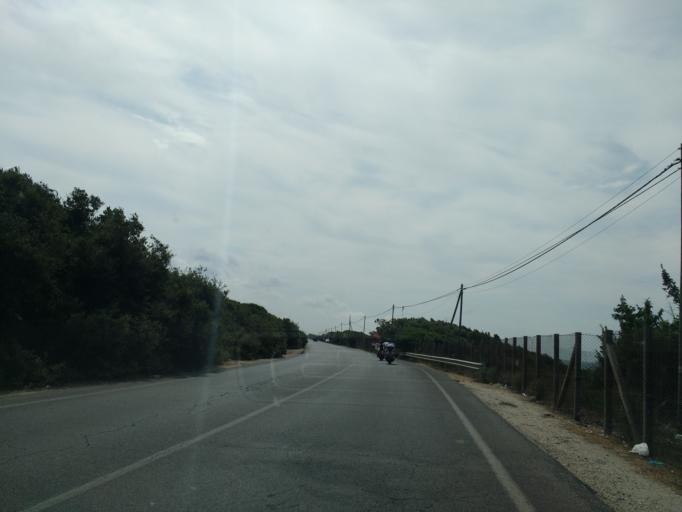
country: IT
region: Latium
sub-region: Citta metropolitana di Roma Capitale
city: Torvaianica
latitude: 41.6845
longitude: 12.3785
